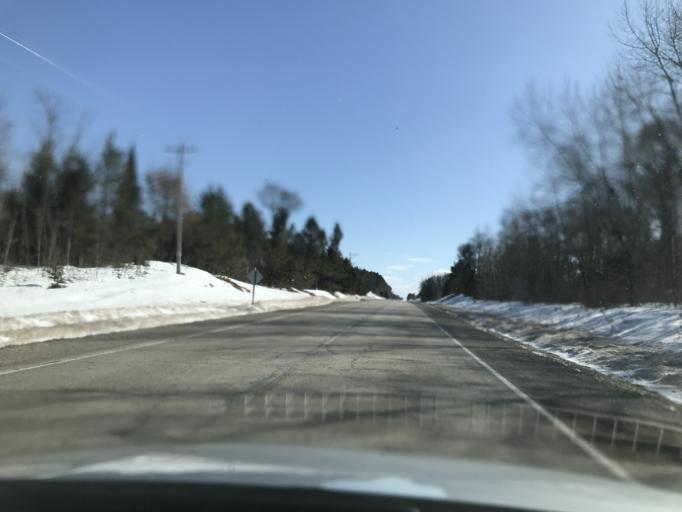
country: US
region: Wisconsin
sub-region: Marinette County
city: Peshtigo
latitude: 45.3300
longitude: -88.1019
